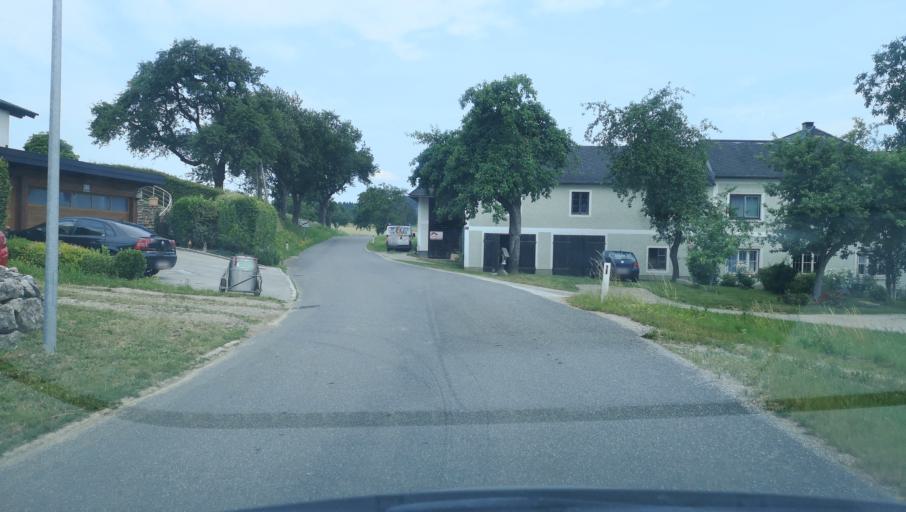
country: AT
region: Lower Austria
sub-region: Politischer Bezirk Melk
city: Blindenmarkt
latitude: 48.1396
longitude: 14.9900
